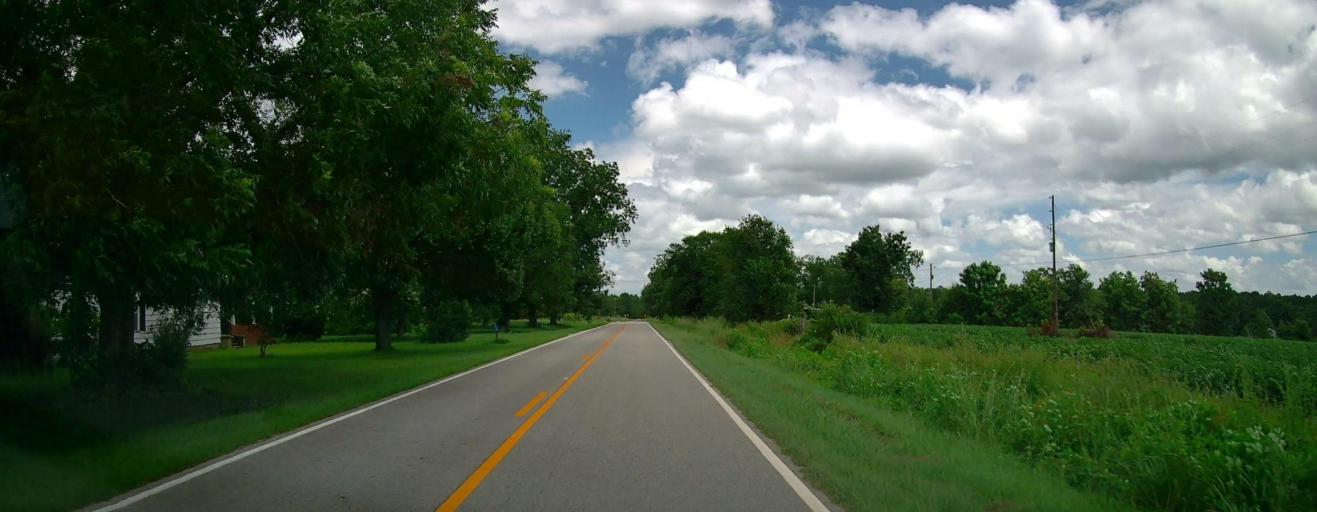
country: US
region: Georgia
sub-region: Irwin County
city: Ocilla
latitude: 31.6444
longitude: -83.2530
